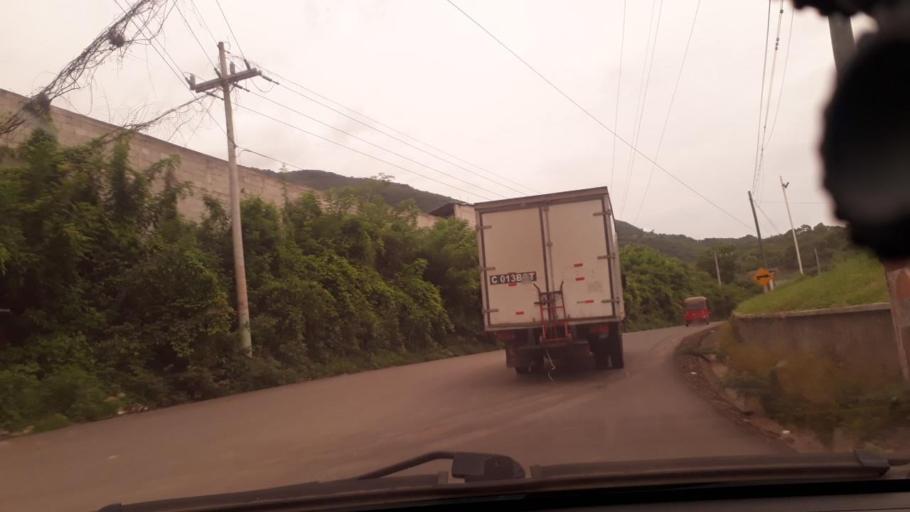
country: GT
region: Chiquimula
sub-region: Municipio de San Juan Ermita
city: San Juan Ermita
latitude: 14.7566
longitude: -89.4402
